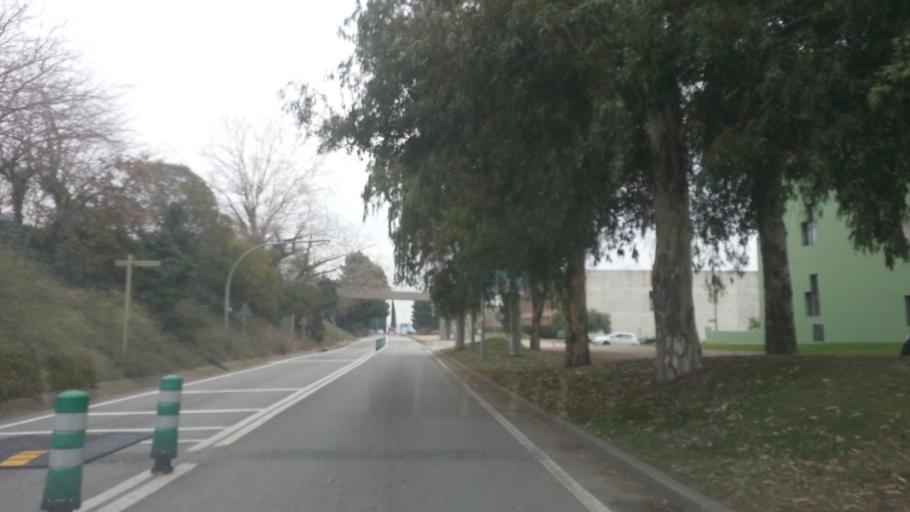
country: ES
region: Catalonia
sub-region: Provincia de Barcelona
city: Barbera del Valles
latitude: 41.5015
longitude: 2.1120
